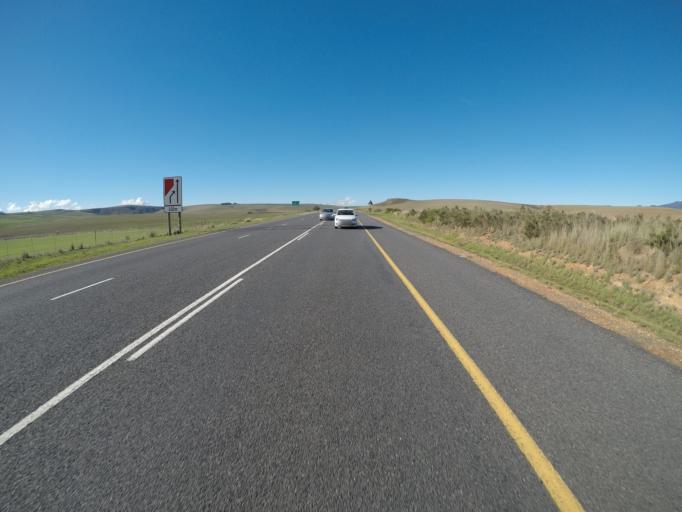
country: ZA
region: Western Cape
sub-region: Overberg District Municipality
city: Hermanus
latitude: -34.2342
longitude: 19.2316
